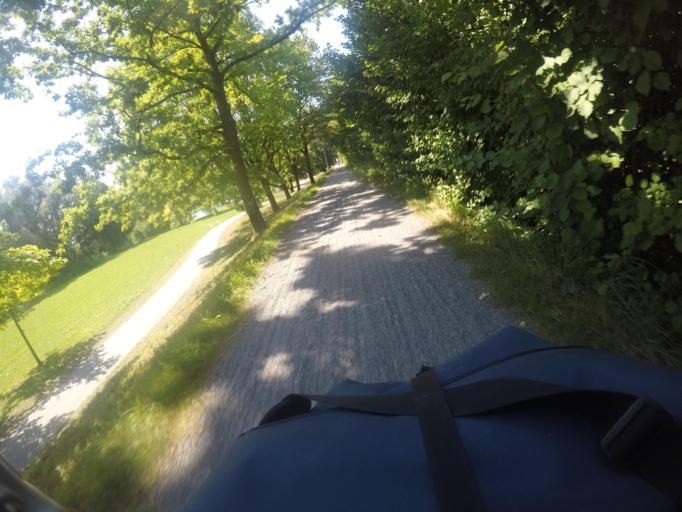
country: CH
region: Saint Gallen
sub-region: Wahlkreis Rheintal
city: Diepoldsau
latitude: 47.3976
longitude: 9.6636
